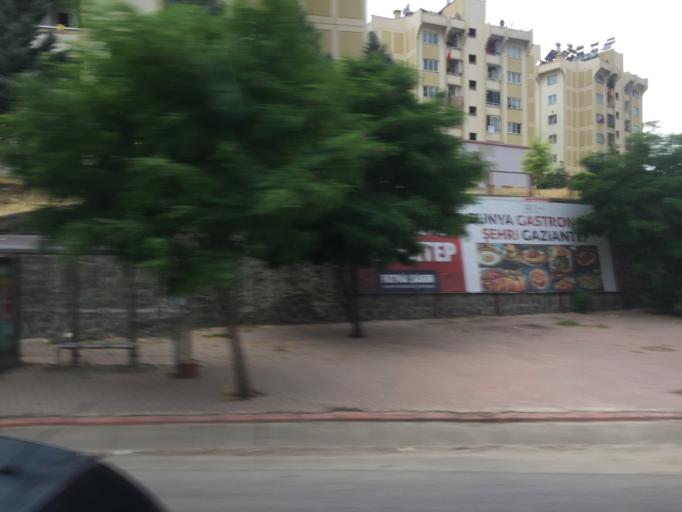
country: TR
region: Gaziantep
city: Gaziantep
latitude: 37.0483
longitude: 37.4226
